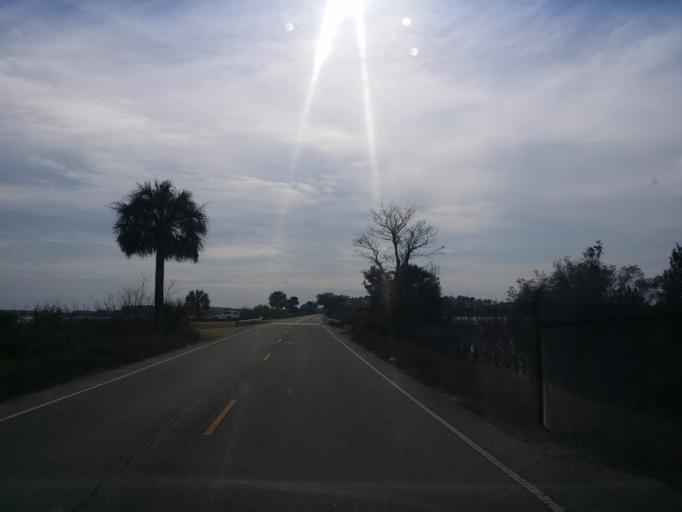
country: US
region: Florida
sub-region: Leon County
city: Woodville
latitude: 30.1309
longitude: -84.1448
